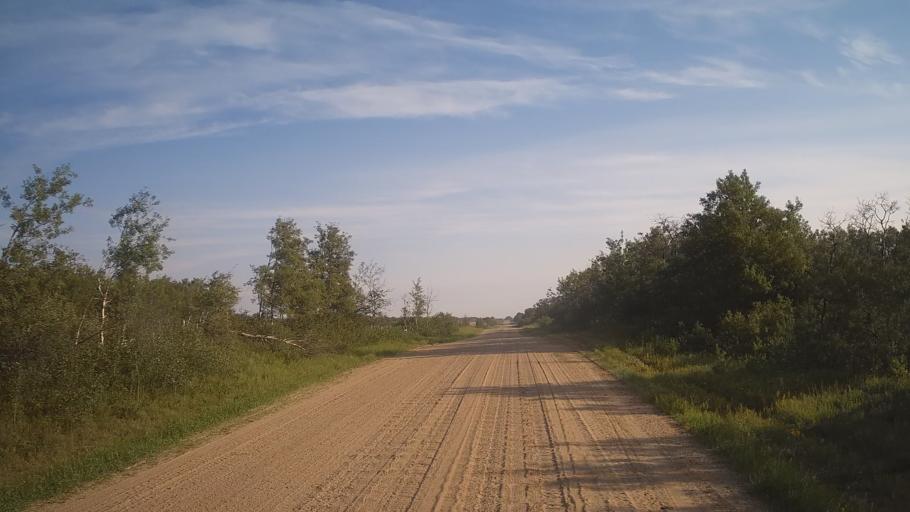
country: CA
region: Saskatchewan
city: Saskatoon
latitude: 51.8476
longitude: -106.5238
